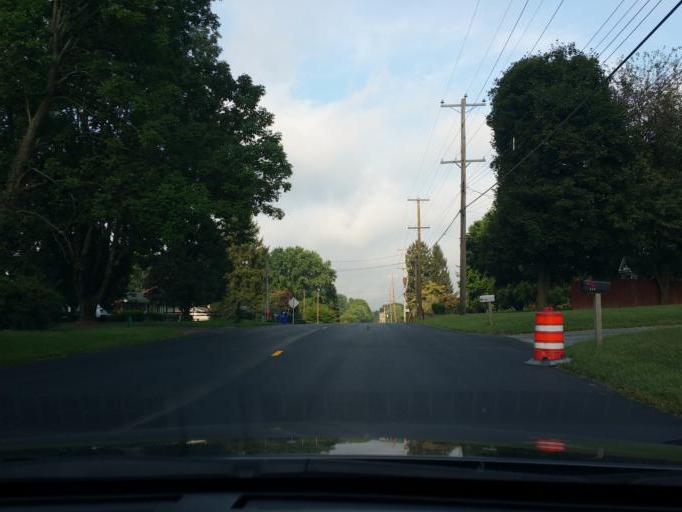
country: US
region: Maryland
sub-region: Cecil County
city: Rising Sun
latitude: 39.6956
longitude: -76.0848
